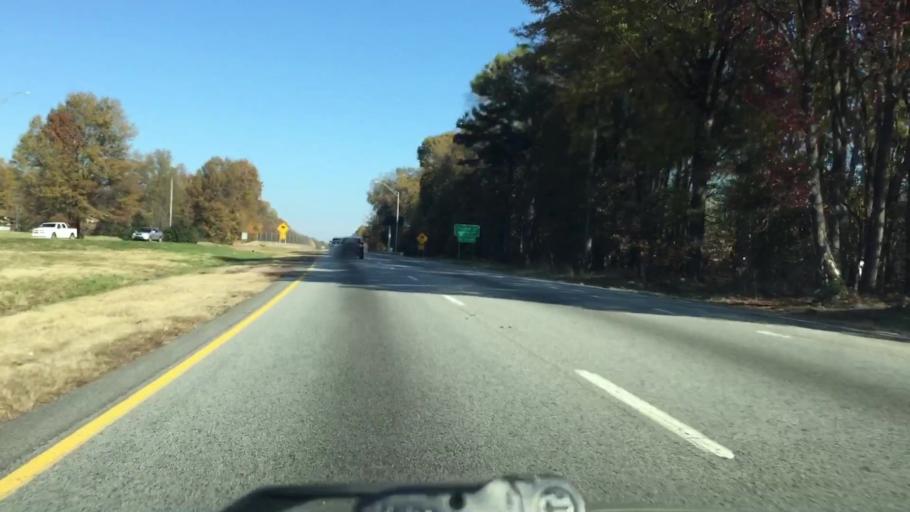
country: US
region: North Carolina
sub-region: Guilford County
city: Greensboro
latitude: 36.0484
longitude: -79.7682
